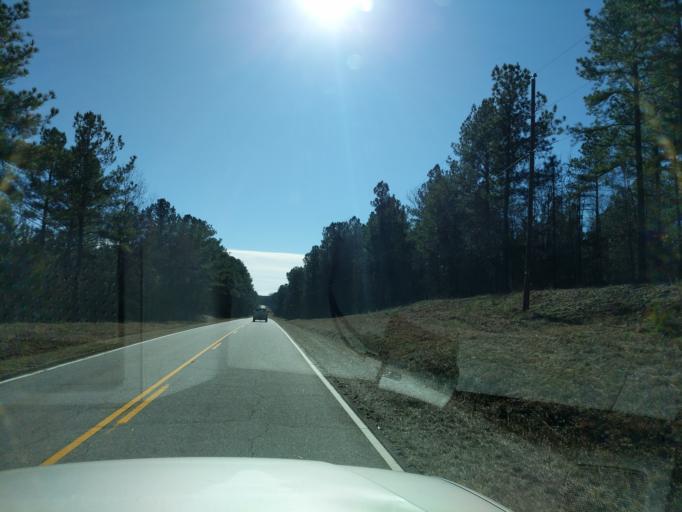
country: US
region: South Carolina
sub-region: Saluda County
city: Saluda
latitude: 34.1353
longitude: -81.8430
